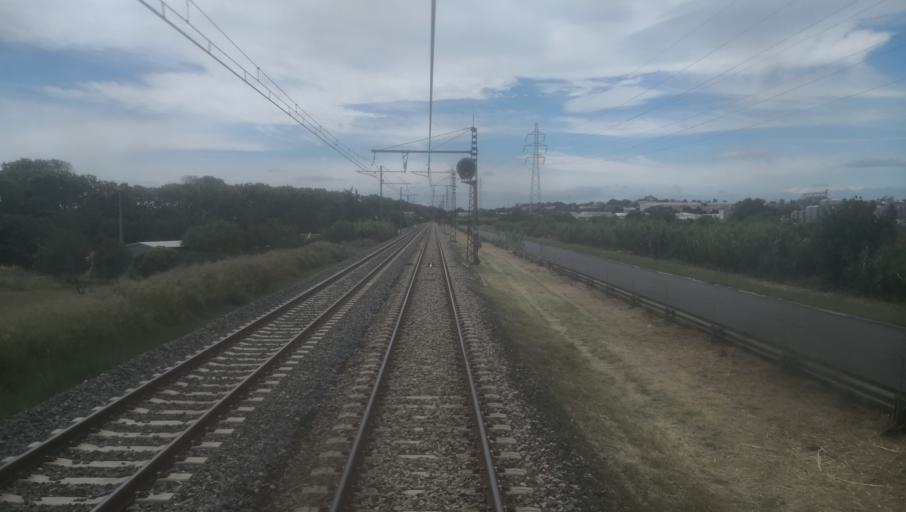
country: FR
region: Languedoc-Roussillon
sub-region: Departement de l'Herault
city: Villeneuve-les-Beziers
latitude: 43.3247
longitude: 3.2687
